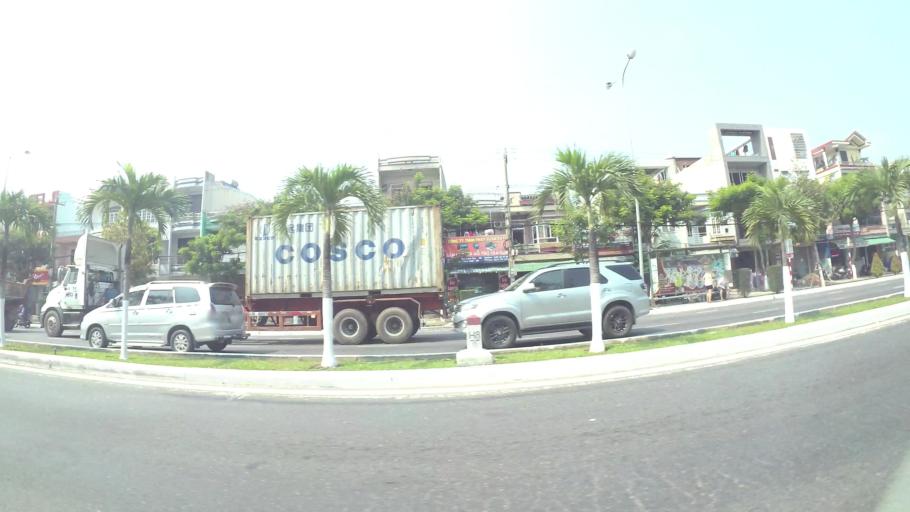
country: VN
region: Da Nang
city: Son Tra
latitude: 16.0427
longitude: 108.2408
